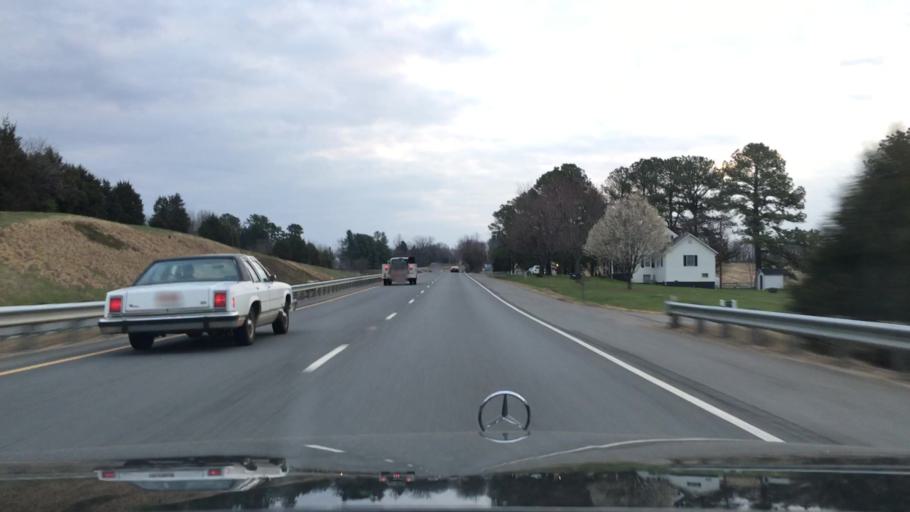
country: US
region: Virginia
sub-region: Madison County
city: Madison
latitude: 38.4003
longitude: -78.2265
